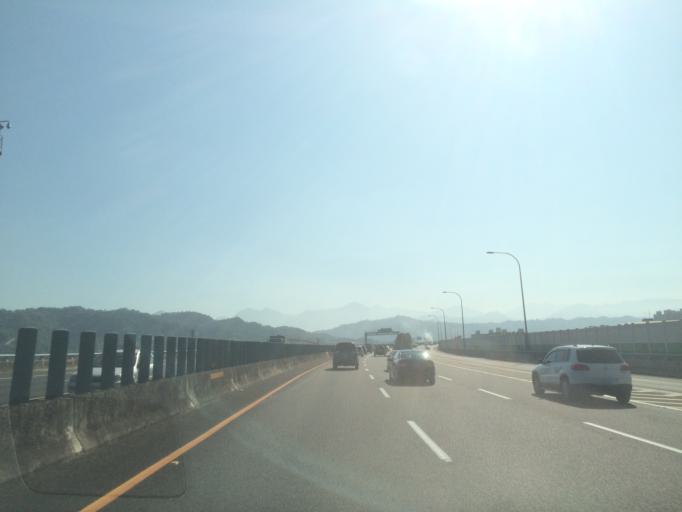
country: TW
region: Taiwan
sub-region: Nantou
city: Nantou
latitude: 23.9191
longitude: 120.6887
